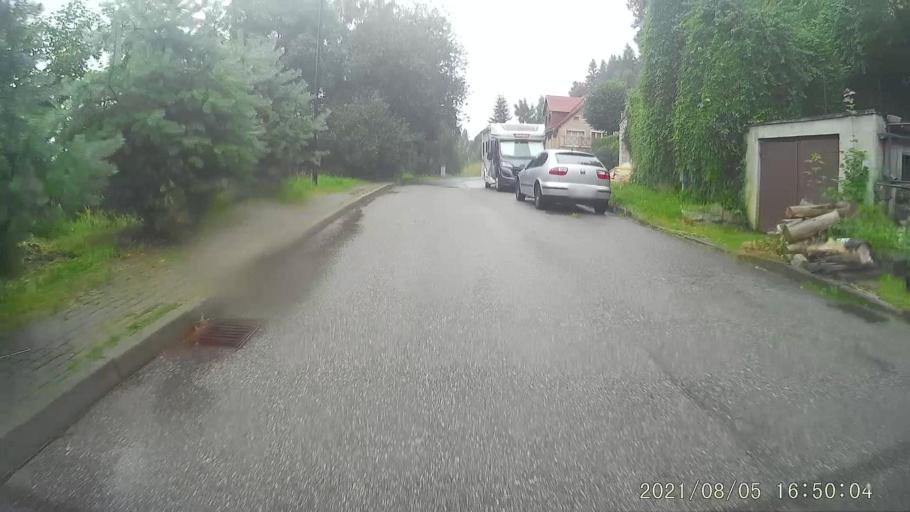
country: PL
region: Lower Silesian Voivodeship
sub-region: Powiat klodzki
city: Duszniki-Zdroj
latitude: 50.3948
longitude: 16.3891
